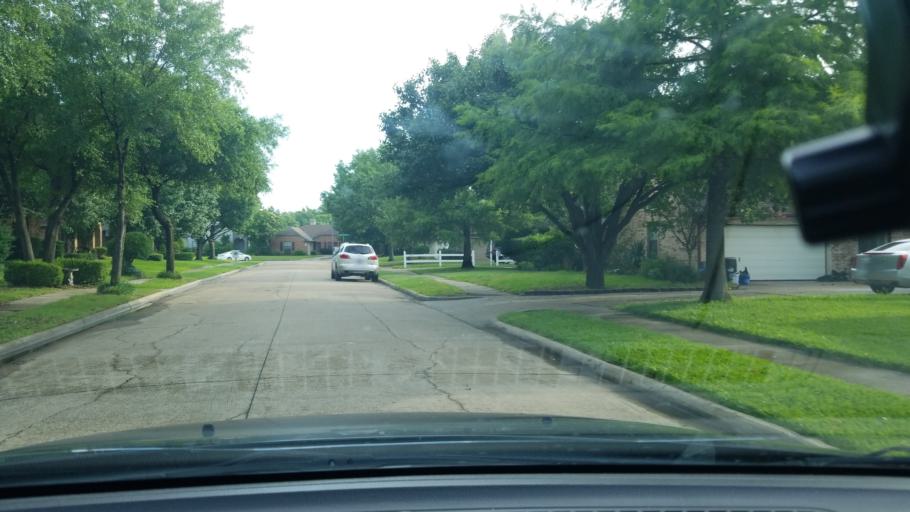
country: US
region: Texas
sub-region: Dallas County
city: Mesquite
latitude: 32.8000
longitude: -96.6002
